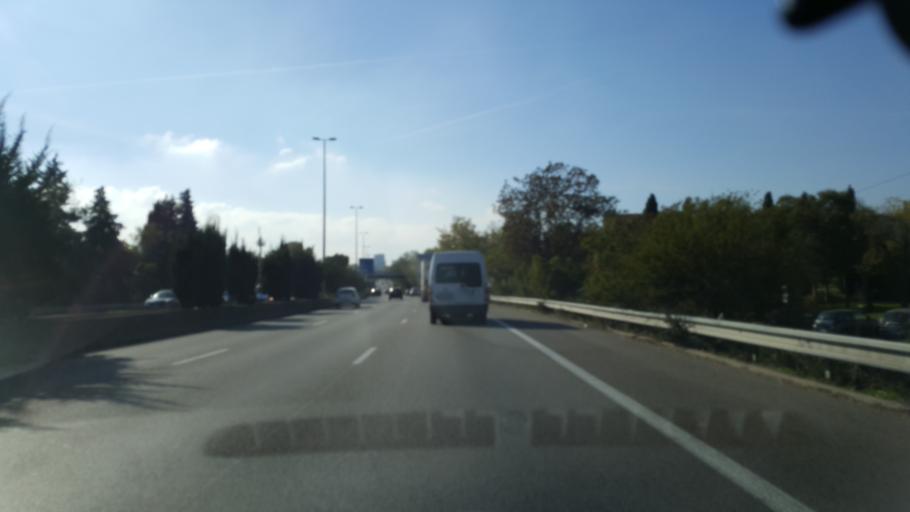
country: FR
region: Provence-Alpes-Cote d'Azur
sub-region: Departement des Bouches-du-Rhone
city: Marseille 11
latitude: 43.2941
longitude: 5.4583
